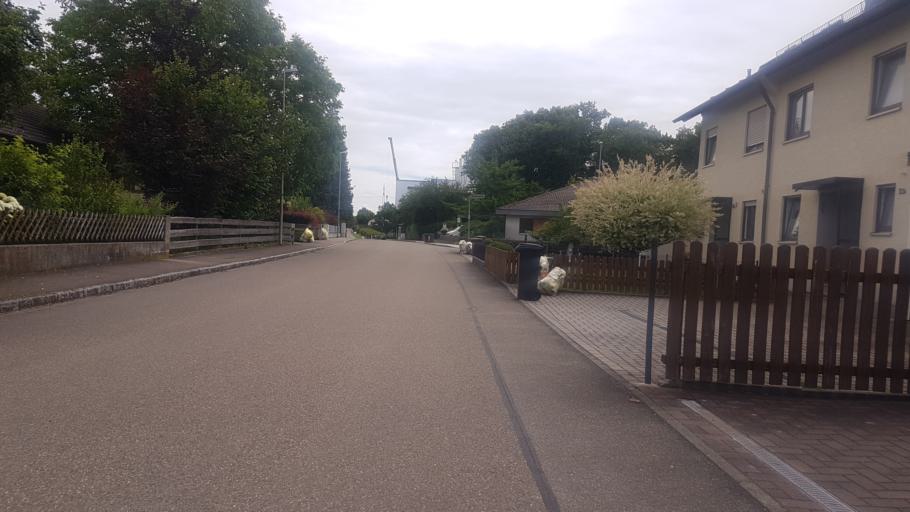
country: DE
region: Bavaria
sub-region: Swabia
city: Lauingen
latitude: 48.5630
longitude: 10.4142
